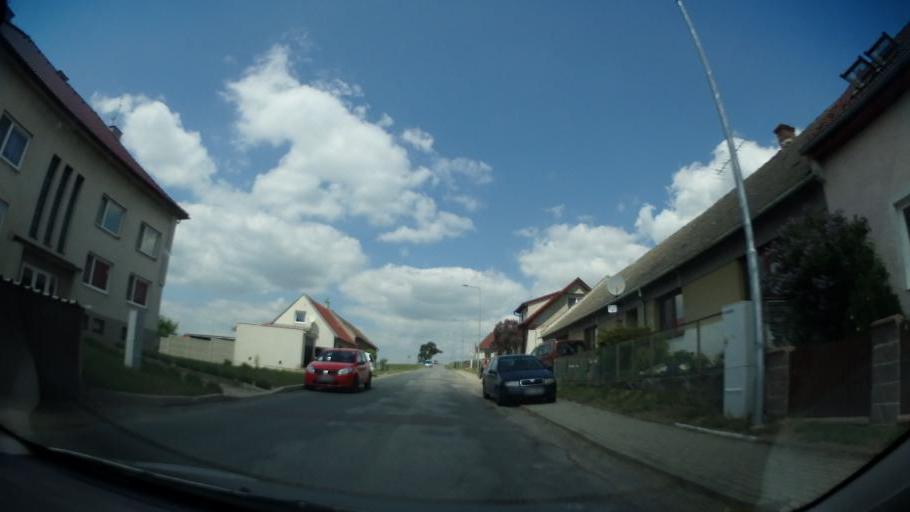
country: CZ
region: Vysocina
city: Hrotovice
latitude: 49.1731
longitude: 16.0862
